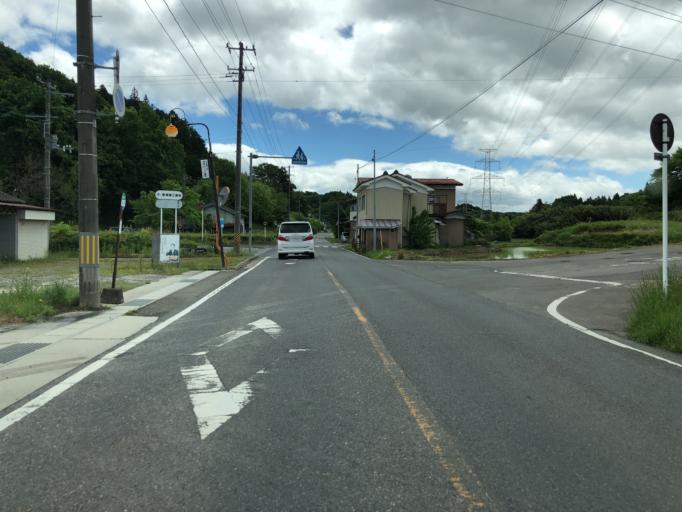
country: JP
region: Fukushima
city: Motomiya
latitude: 37.5098
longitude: 140.4307
